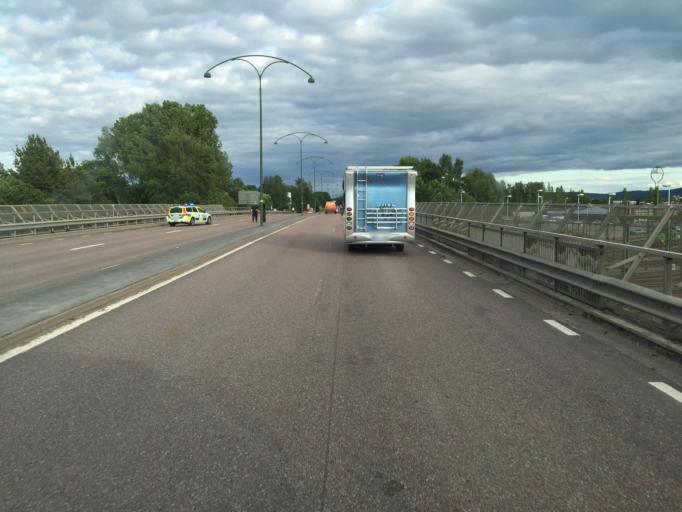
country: SE
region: Dalarna
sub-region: Borlange Kommun
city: Borlaenge
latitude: 60.4823
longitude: 15.4242
